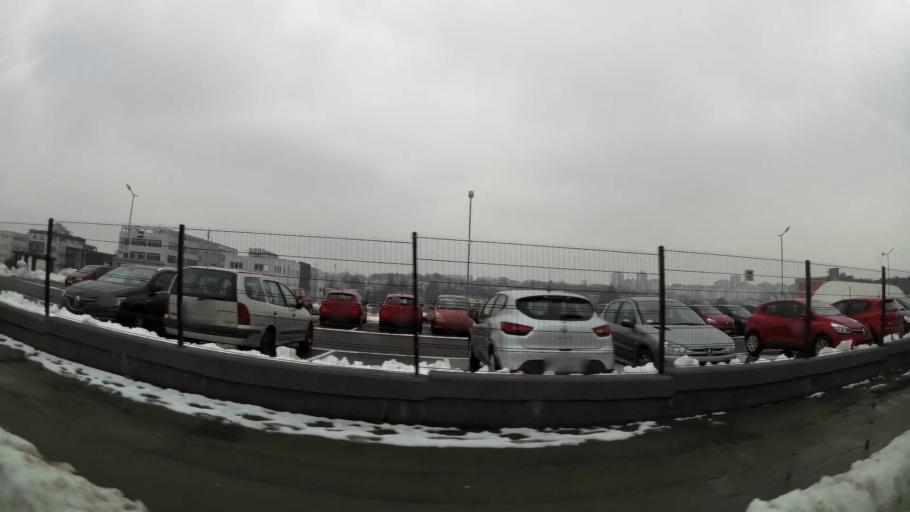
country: RS
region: Central Serbia
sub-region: Belgrade
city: Vozdovac
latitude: 44.7671
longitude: 20.4856
